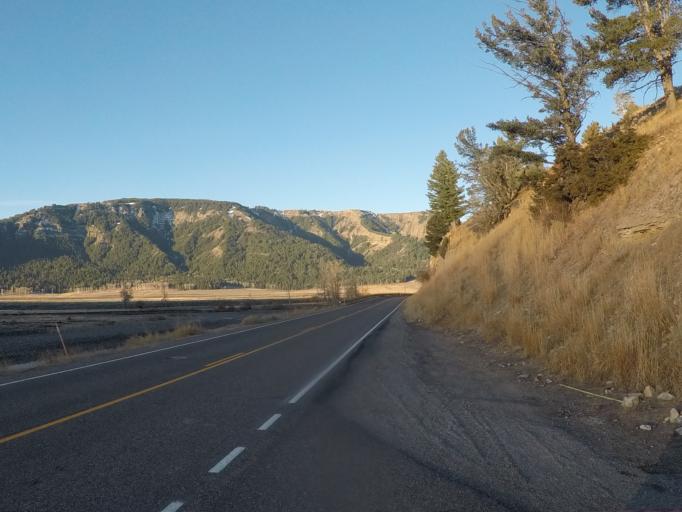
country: US
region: Montana
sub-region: Park County
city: Livingston
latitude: 44.8701
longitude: -110.1778
